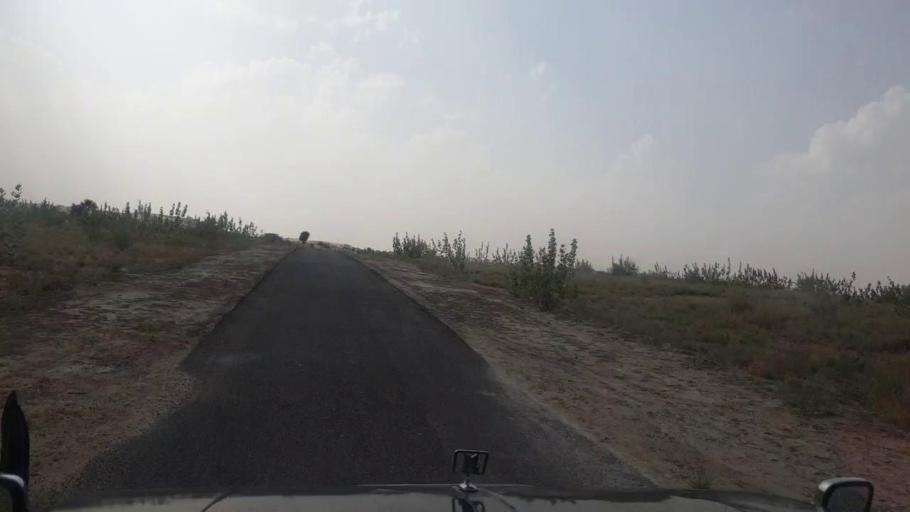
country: PK
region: Sindh
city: Islamkot
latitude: 25.2292
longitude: 70.2829
